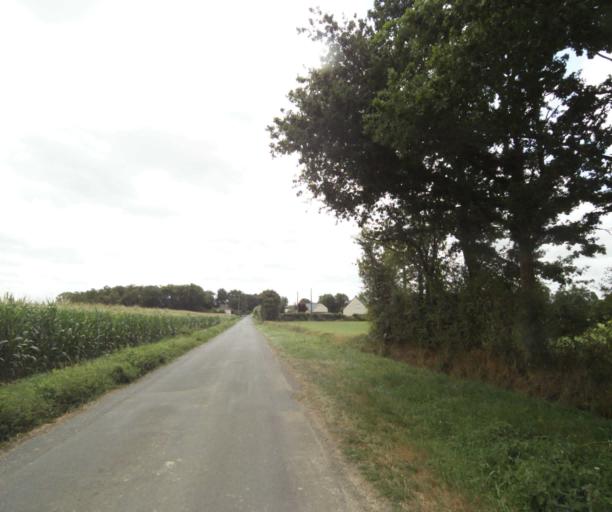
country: FR
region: Pays de la Loire
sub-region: Departement de la Sarthe
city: Sable-sur-Sarthe
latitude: 47.8600
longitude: -0.3565
